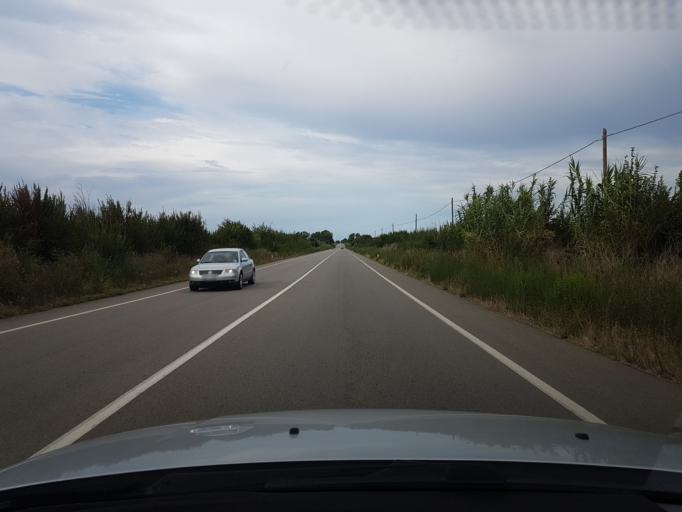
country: IT
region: Sardinia
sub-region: Provincia di Oristano
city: Nuraxinieddu
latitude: 39.9511
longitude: 8.6087
